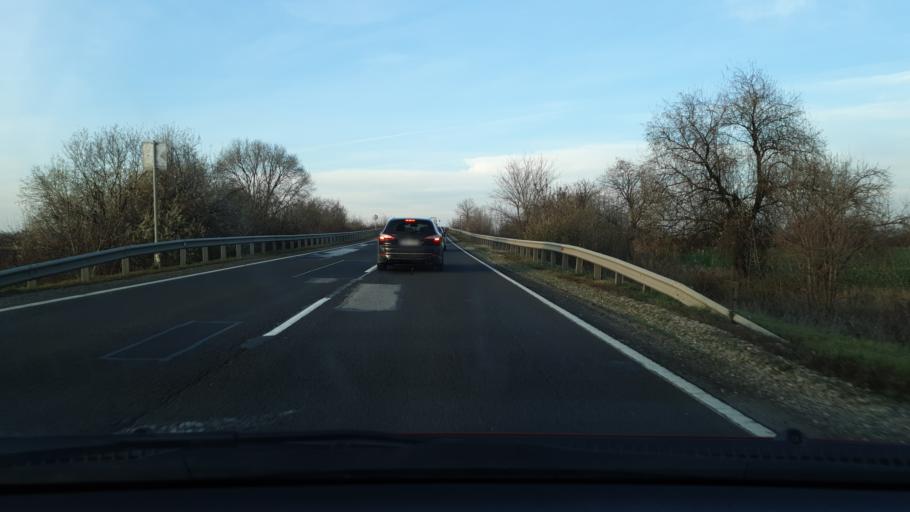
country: HU
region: Jasz-Nagykun-Szolnok
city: Toszeg
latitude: 47.1717
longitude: 20.1032
